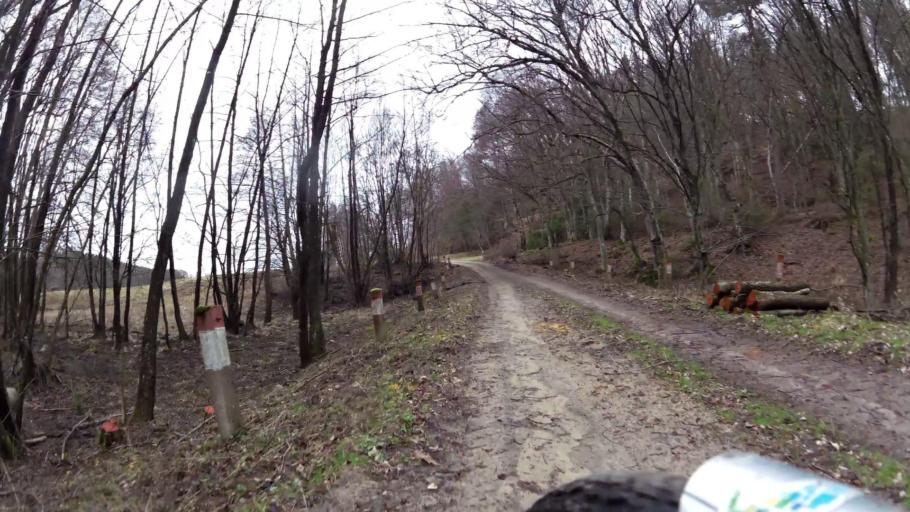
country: PL
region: Pomeranian Voivodeship
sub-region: Powiat bytowski
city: Kolczyglowy
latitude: 54.2510
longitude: 17.3025
